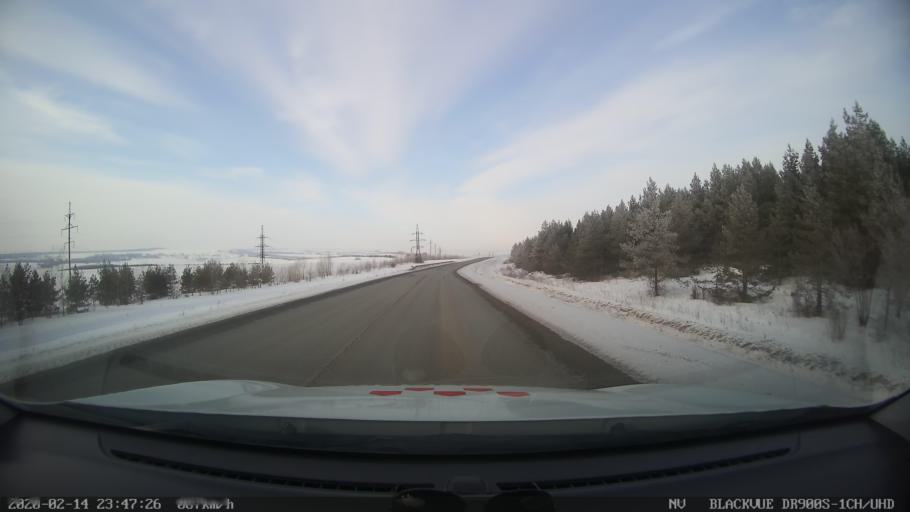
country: RU
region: Tatarstan
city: Kuybyshevskiy Zaton
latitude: 55.2385
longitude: 49.2090
